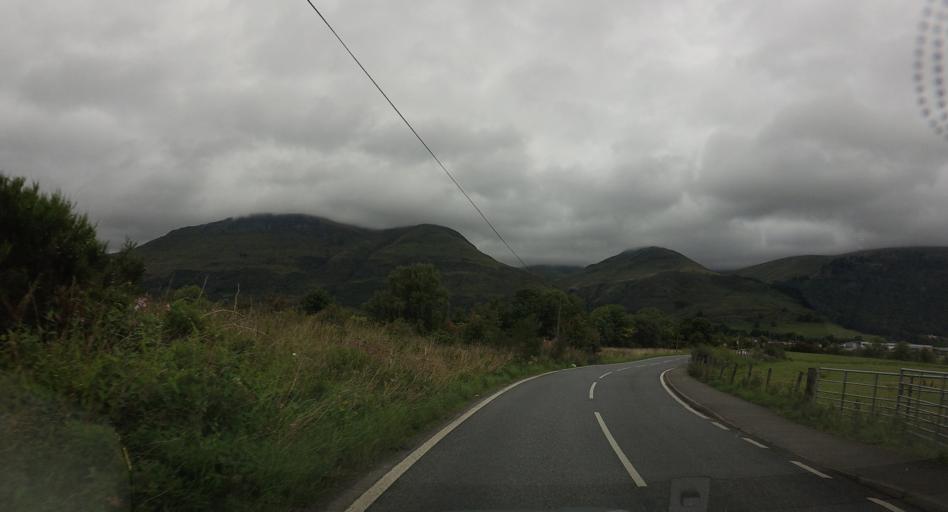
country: GB
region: Scotland
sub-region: Clackmannanshire
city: Alva
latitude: 56.1455
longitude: -3.7982
